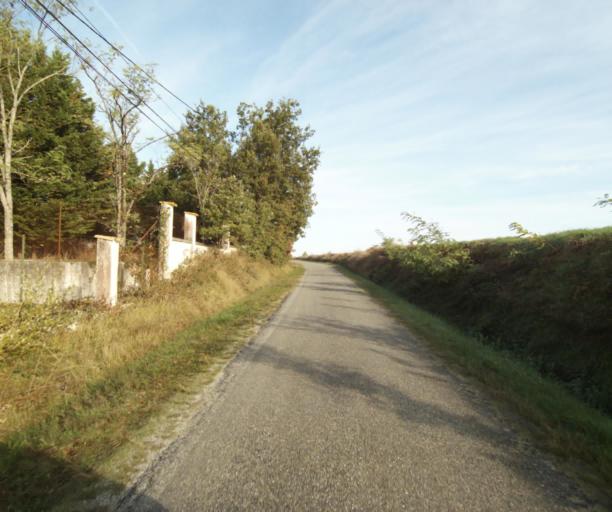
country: FR
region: Midi-Pyrenees
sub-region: Departement de la Haute-Garonne
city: Villemur-sur-Tarn
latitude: 43.9046
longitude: 1.5160
